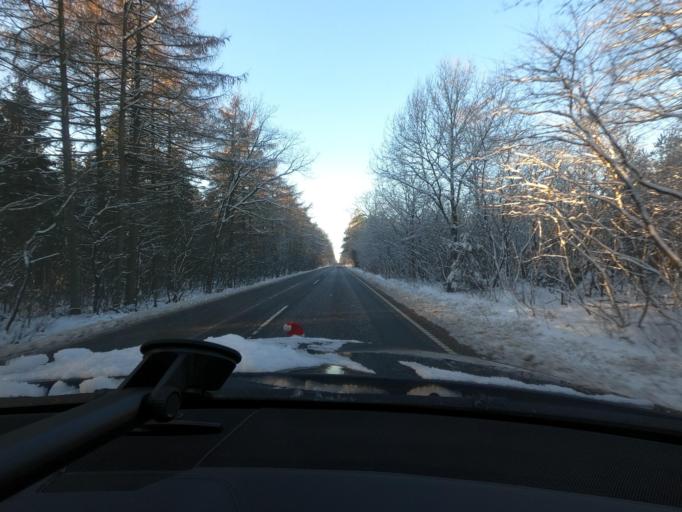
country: DK
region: South Denmark
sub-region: Tonder Kommune
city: Logumkloster
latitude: 55.1755
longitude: 8.9398
